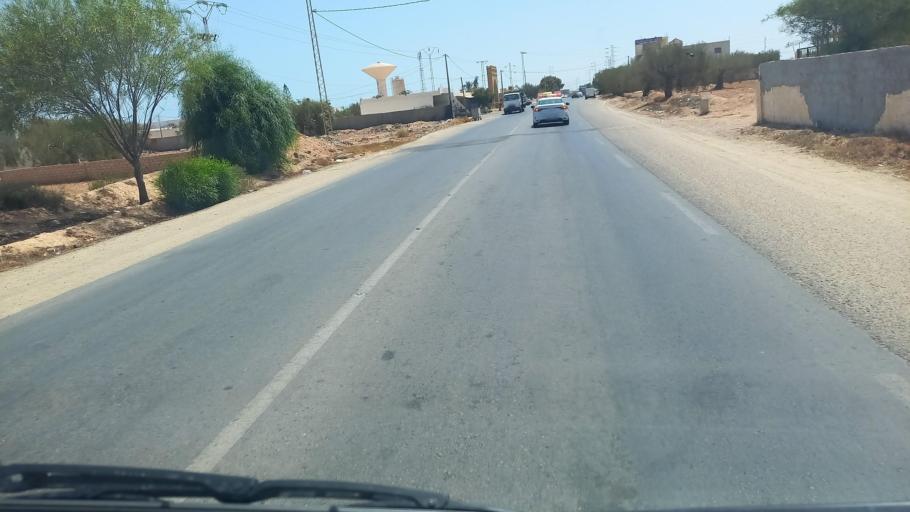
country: TN
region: Madanin
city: Zarzis
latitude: 33.5424
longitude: 11.0760
